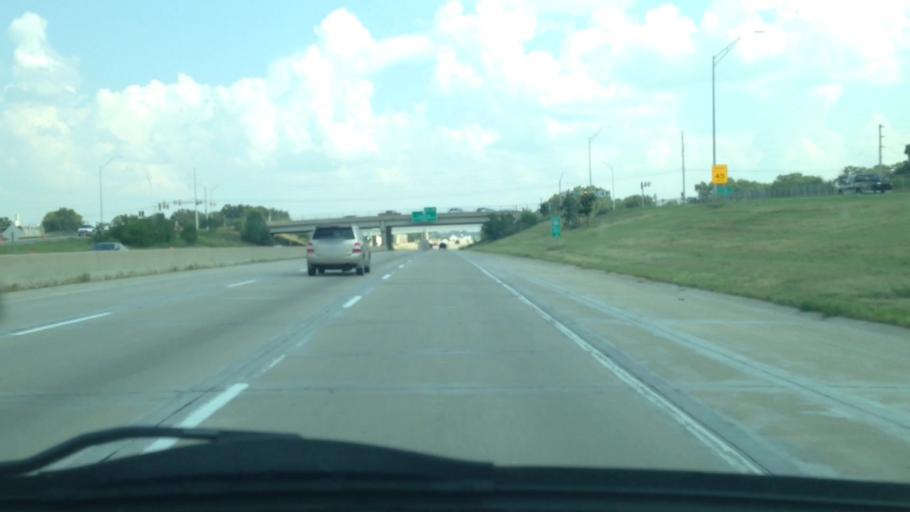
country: US
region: Iowa
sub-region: Black Hawk County
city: Waterloo
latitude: 42.5096
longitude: -92.3778
